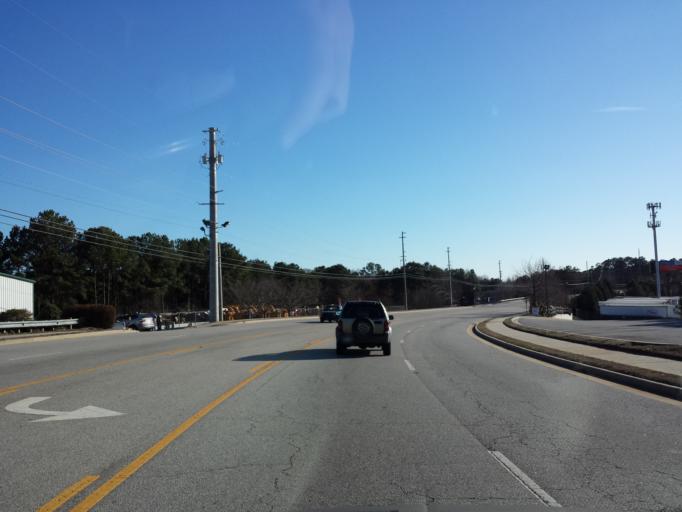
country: US
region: Georgia
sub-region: Cobb County
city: Marietta
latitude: 33.9583
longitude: -84.5138
